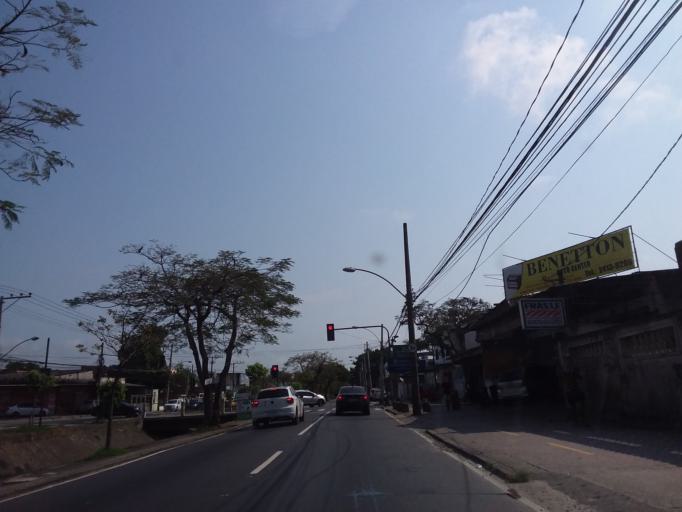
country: BR
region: Rio de Janeiro
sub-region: Nilopolis
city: Nilopolis
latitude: -22.8988
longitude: -43.5415
